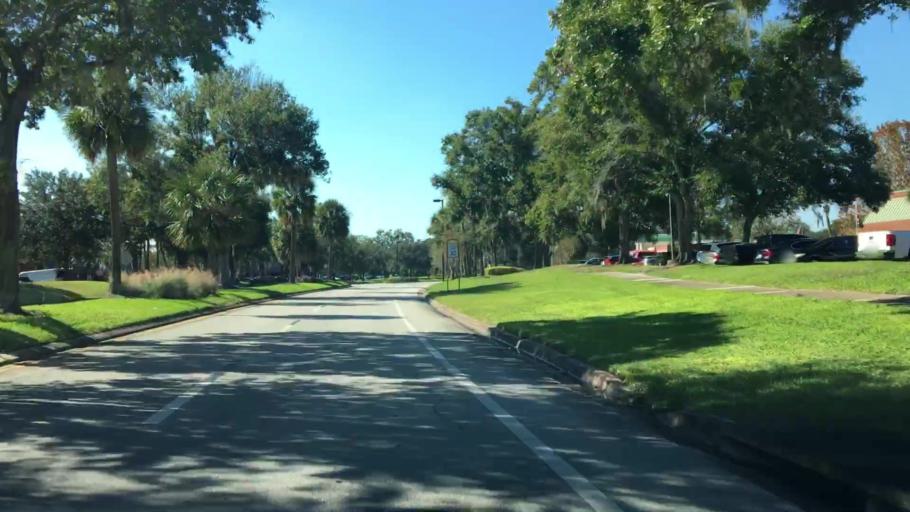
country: US
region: Florida
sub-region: Orange County
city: Conway
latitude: 28.4591
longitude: -81.2970
